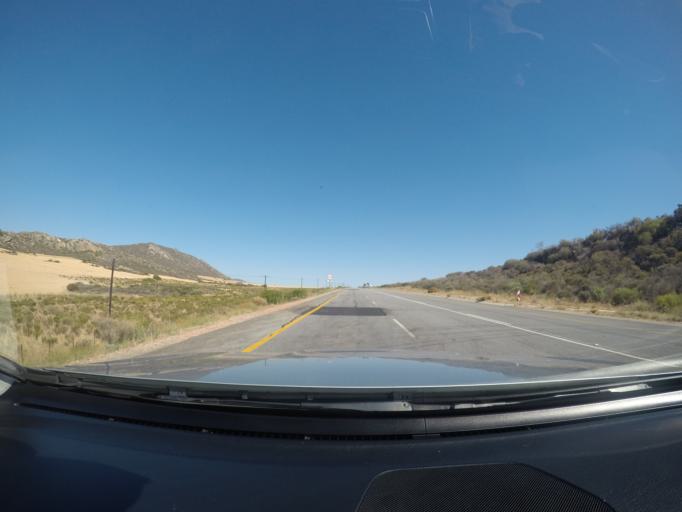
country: ZA
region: Western Cape
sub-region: West Coast District Municipality
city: Clanwilliam
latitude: -32.2938
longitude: 18.8991
